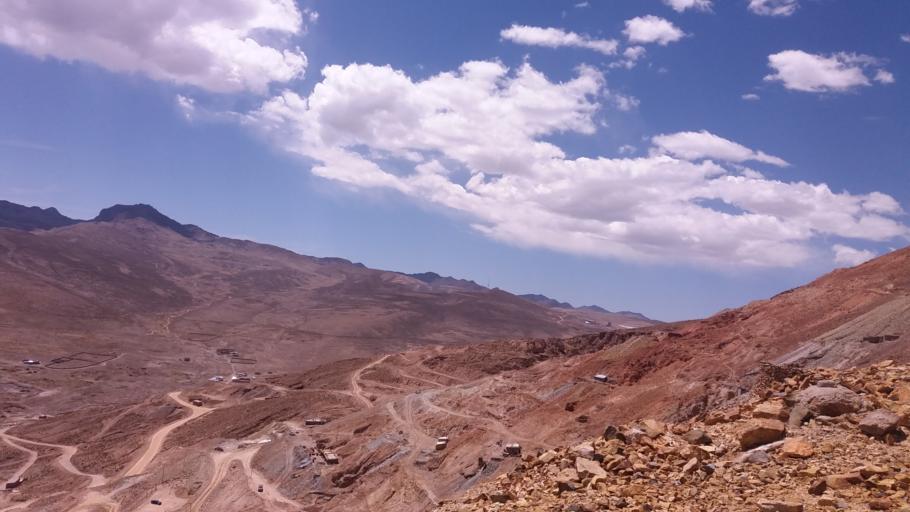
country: BO
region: Potosi
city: Potosi
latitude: -19.6138
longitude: -65.7458
